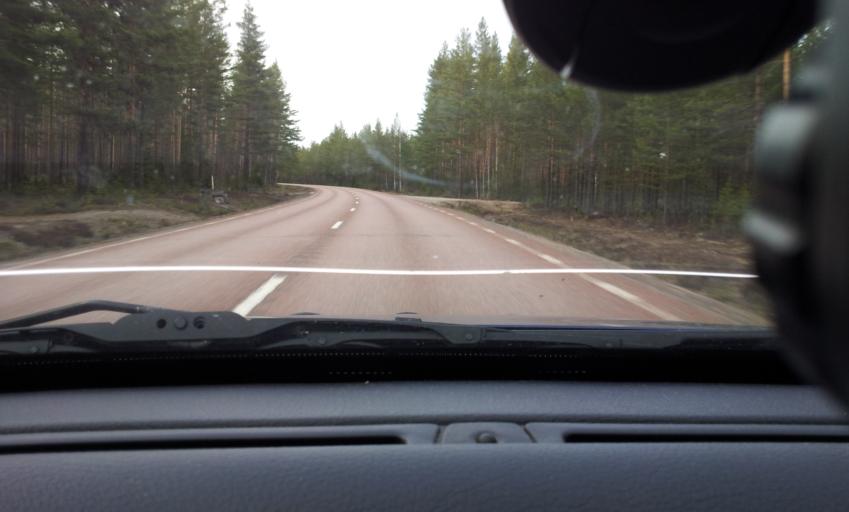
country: SE
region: Gaevleborg
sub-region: Ljusdals Kommun
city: Farila
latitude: 61.8479
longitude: 15.7516
